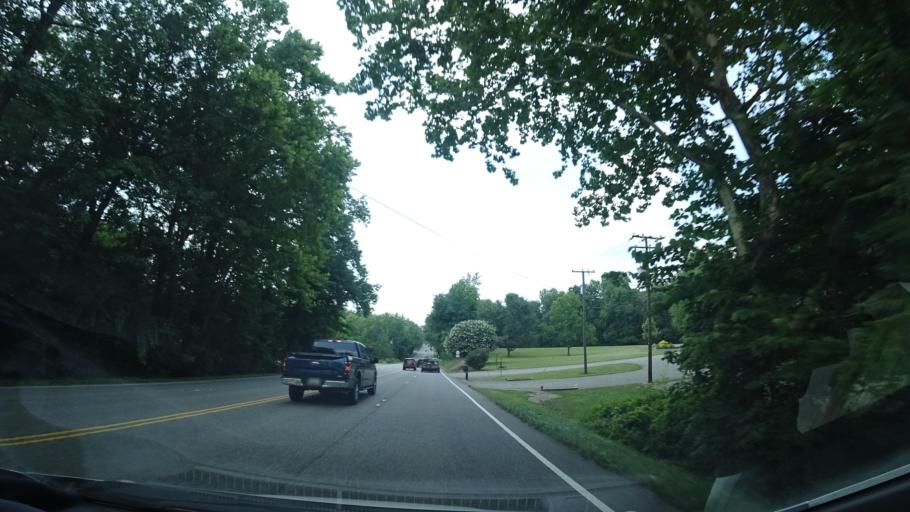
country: US
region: Virginia
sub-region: Hanover County
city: Ashland
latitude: 37.7973
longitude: -77.4720
